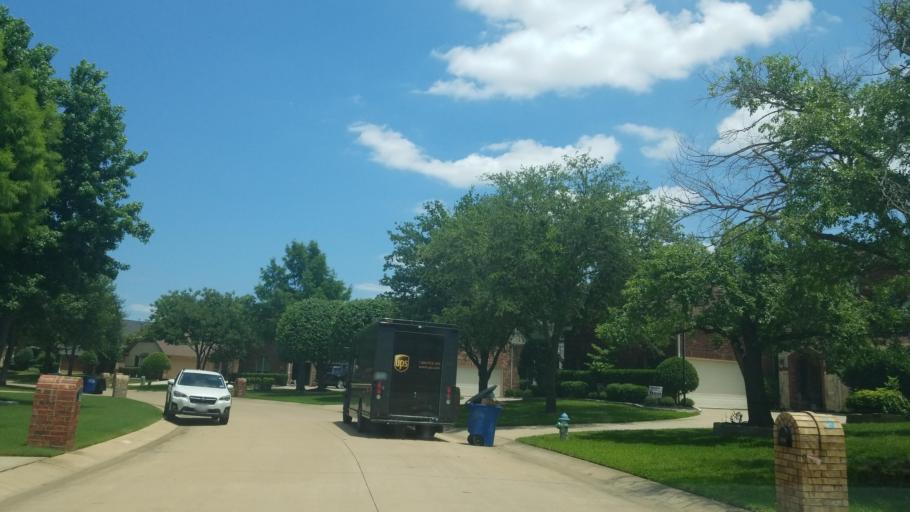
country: US
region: Texas
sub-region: Denton County
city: Copper Canyon
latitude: 33.0771
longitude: -97.0842
